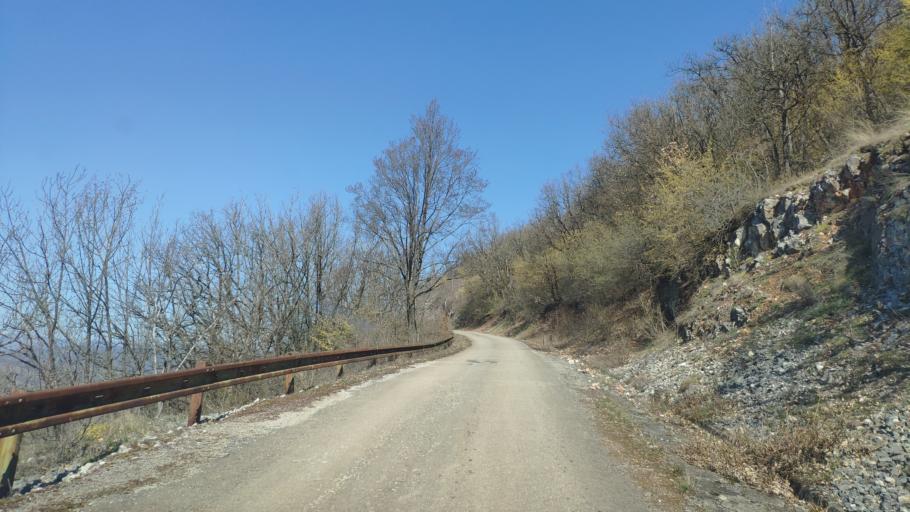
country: SK
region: Kosicky
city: Roznava
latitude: 48.5777
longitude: 20.4052
